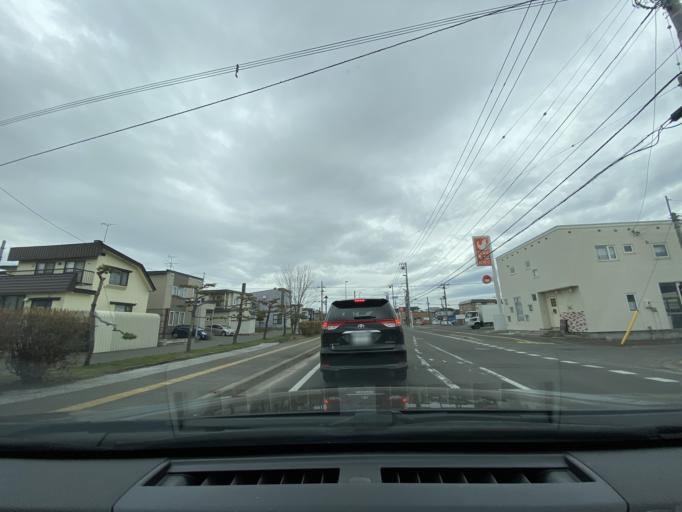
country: JP
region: Hokkaido
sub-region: Asahikawa-shi
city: Asahikawa
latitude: 43.7925
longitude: 142.4168
